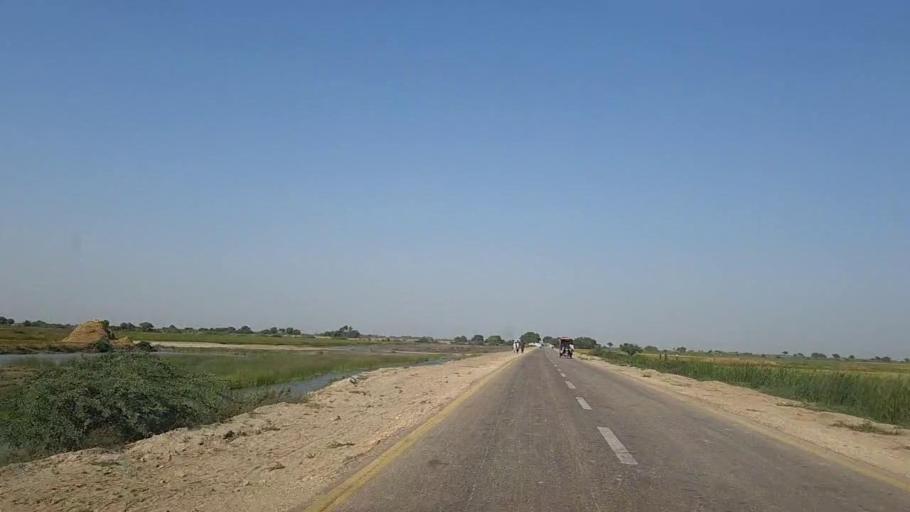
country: PK
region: Sindh
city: Jati
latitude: 24.4115
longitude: 68.3003
